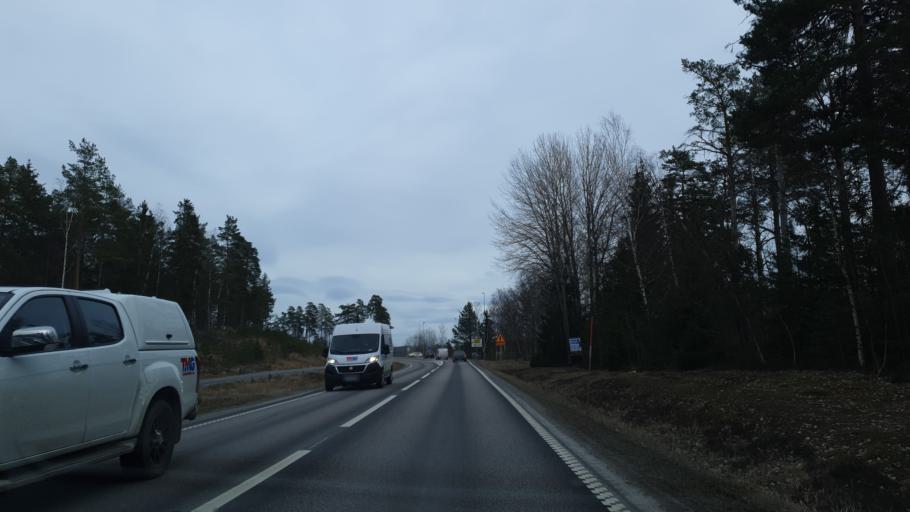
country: SE
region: Stockholm
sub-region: Vallentuna Kommun
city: Vallentuna
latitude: 59.5304
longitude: 18.1045
